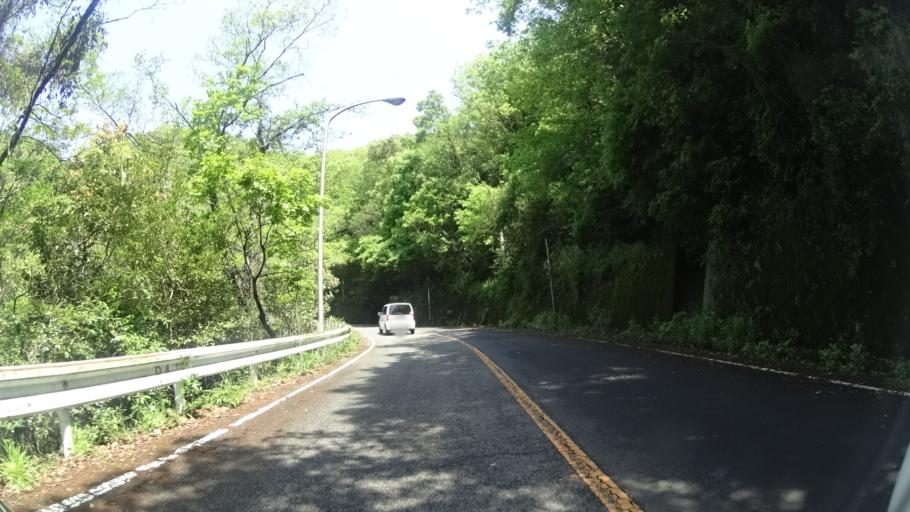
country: JP
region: Tokushima
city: Tokushima-shi
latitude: 34.0653
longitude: 134.5359
